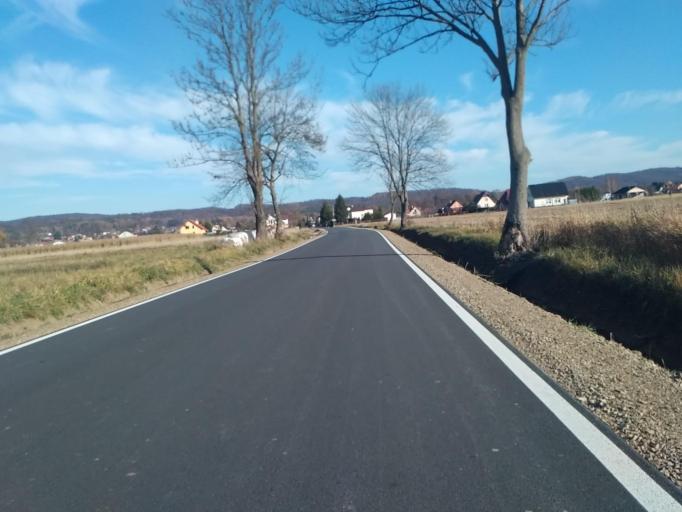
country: PL
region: Subcarpathian Voivodeship
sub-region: Powiat brzozowski
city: Humniska
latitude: 49.6706
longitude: 22.0403
